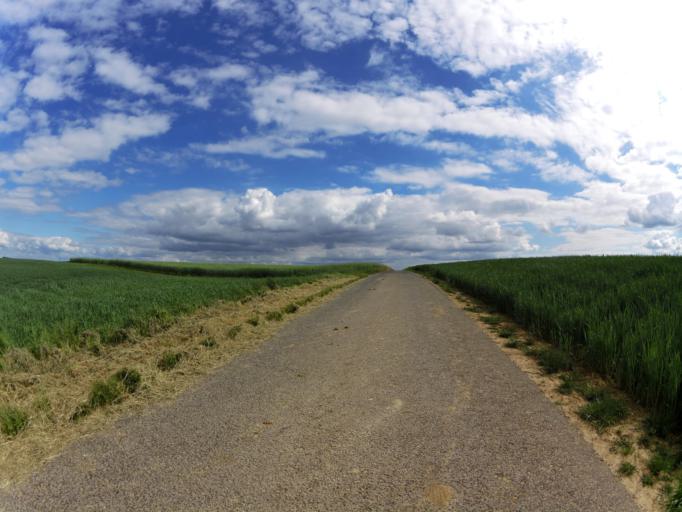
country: DE
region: Bavaria
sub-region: Regierungsbezirk Unterfranken
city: Gaukonigshofen
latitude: 49.6531
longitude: 10.0102
